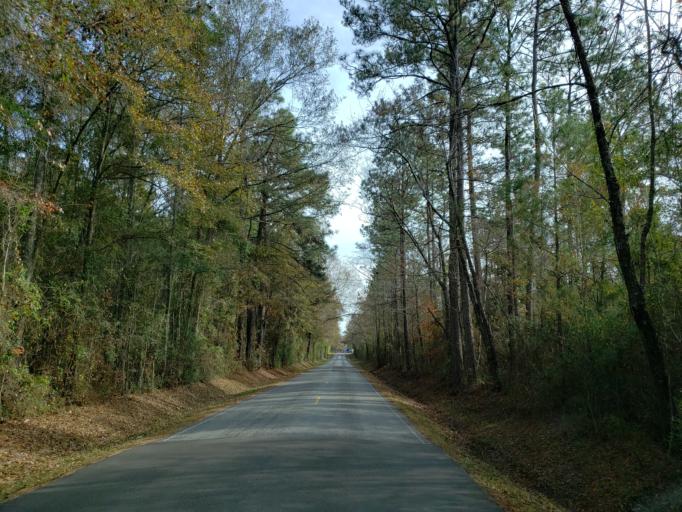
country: US
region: Mississippi
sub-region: Forrest County
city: Rawls Springs
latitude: 31.4029
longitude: -89.3965
